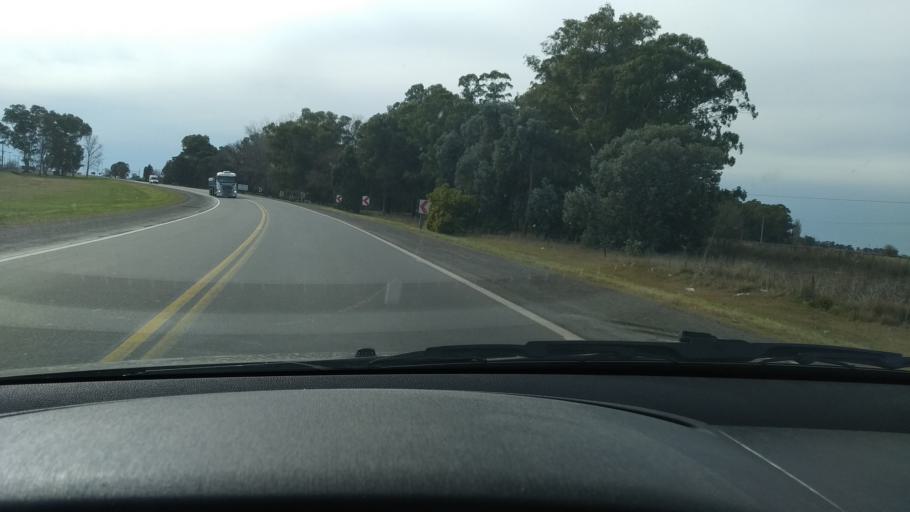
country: AR
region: Buenos Aires
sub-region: Partido de Azul
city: Azul
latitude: -36.7627
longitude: -59.8061
